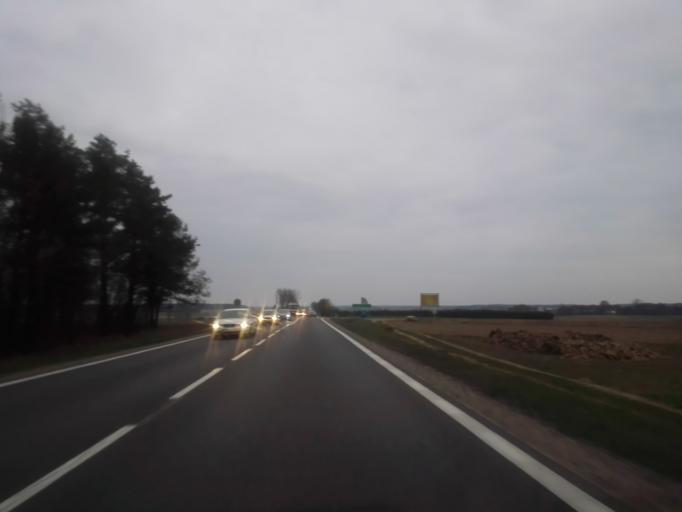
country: PL
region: Podlasie
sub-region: Powiat kolnenski
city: Stawiski
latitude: 53.4326
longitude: 22.1721
